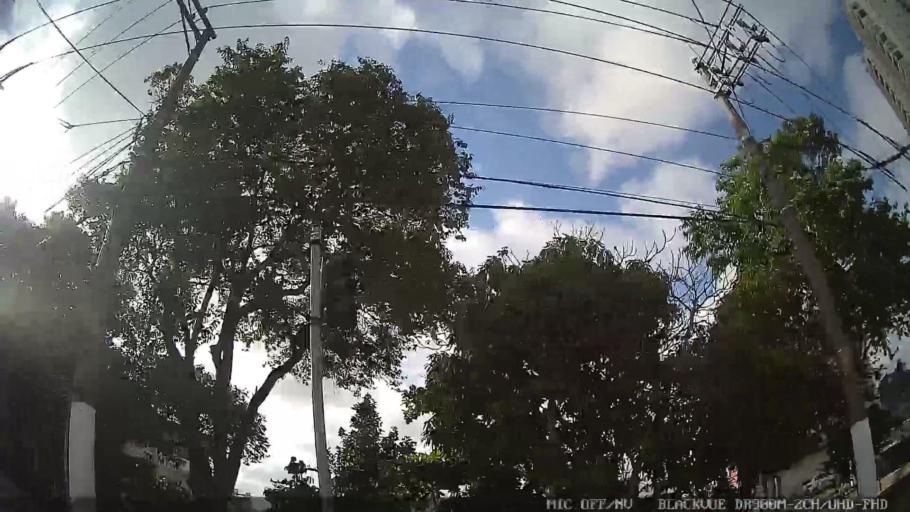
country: BR
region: Sao Paulo
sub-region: Sao Caetano Do Sul
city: Sao Caetano do Sul
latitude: -23.5728
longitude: -46.5327
